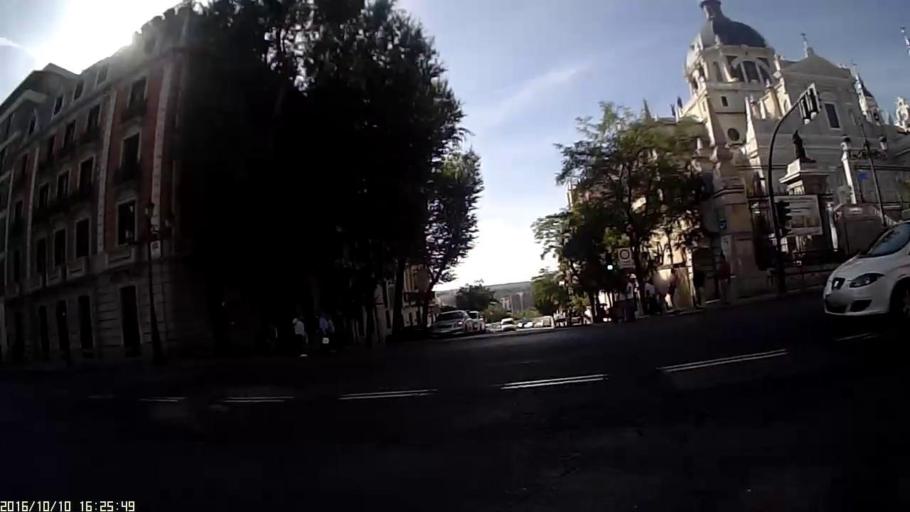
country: ES
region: Madrid
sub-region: Provincia de Madrid
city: Madrid
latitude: 40.4150
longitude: -3.7135
